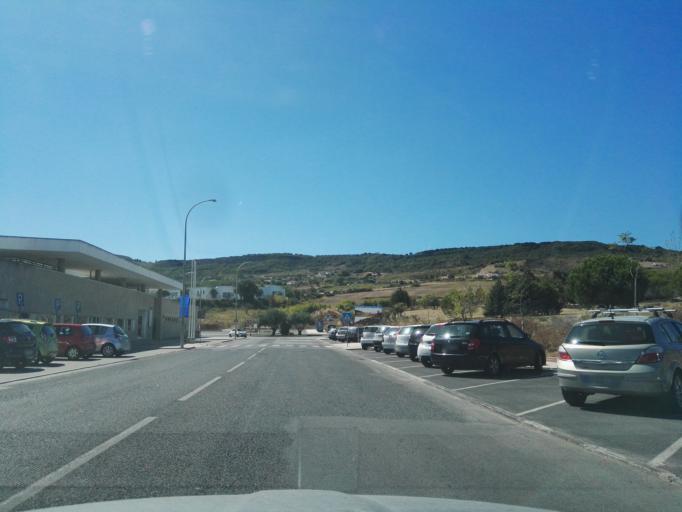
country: PT
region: Lisbon
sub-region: Arruda Dos Vinhos
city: Arruda dos Vinhos
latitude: 38.9820
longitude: -9.0809
